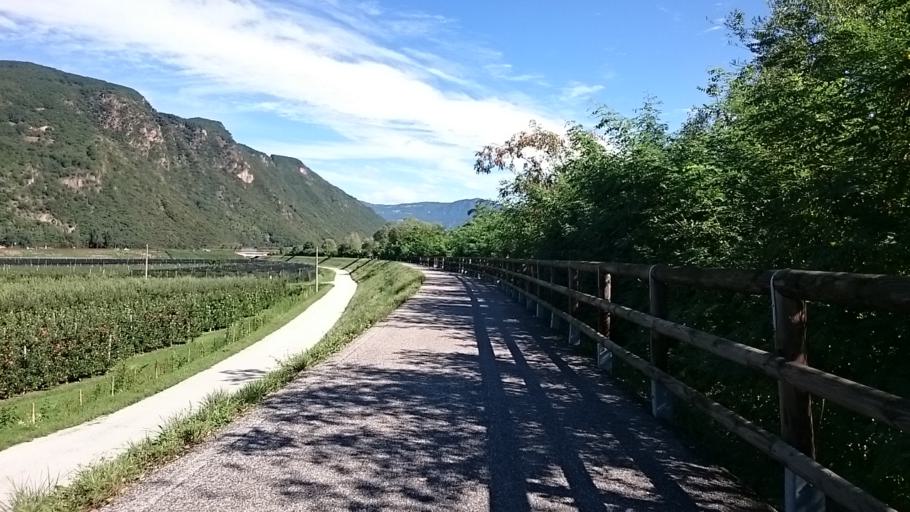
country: IT
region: Trentino-Alto Adige
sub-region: Bolzano
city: Vadena
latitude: 46.4159
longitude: 11.3149
